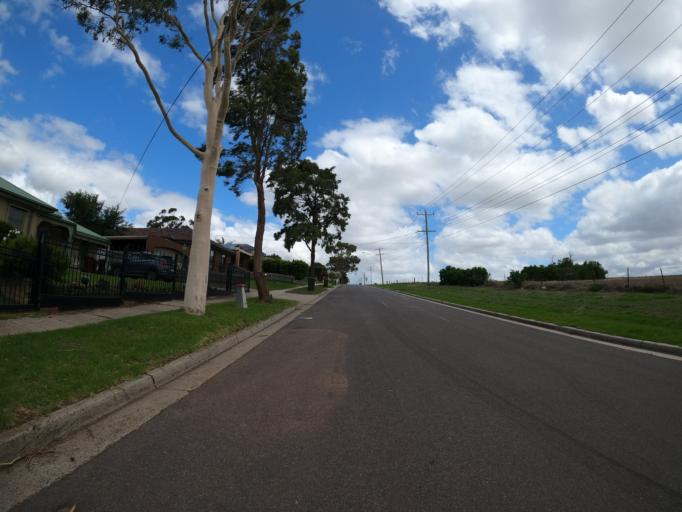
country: AU
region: Victoria
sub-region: Hume
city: Westmeadows
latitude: -37.6767
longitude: 144.8725
